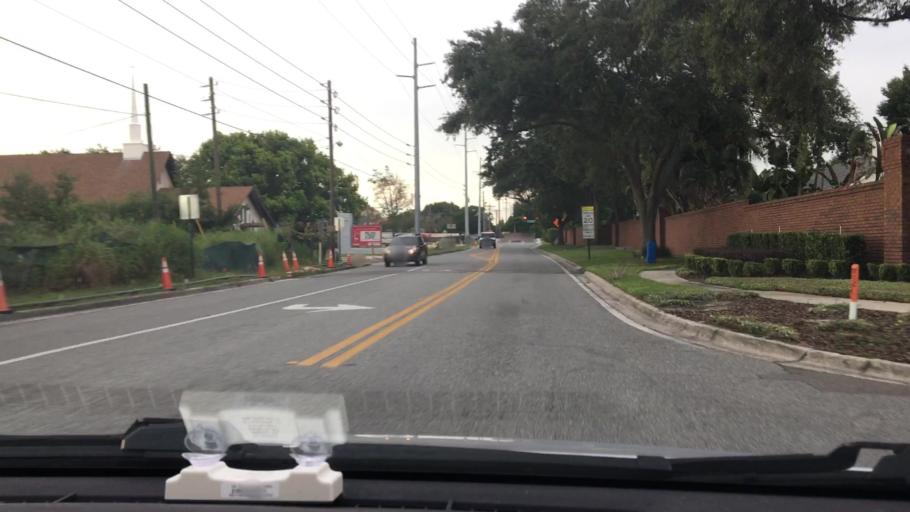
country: US
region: Florida
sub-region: Orange County
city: Eatonville
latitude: 28.6380
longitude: -81.3862
